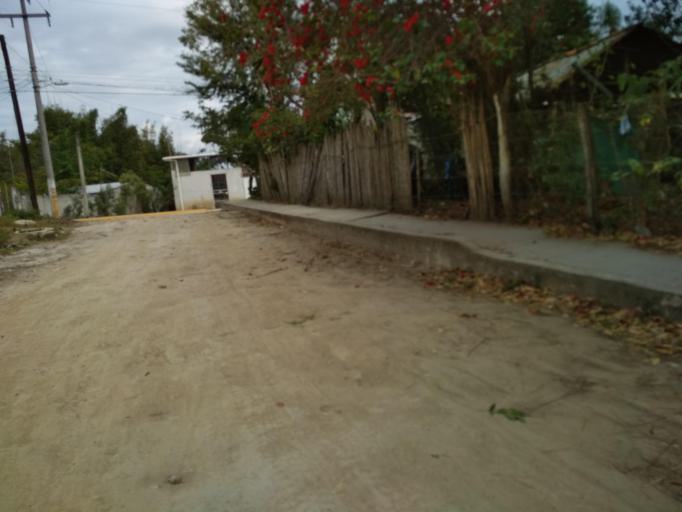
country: MX
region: Veracruz
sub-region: Coatepec
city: Tuzamapan
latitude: 19.3686
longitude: -96.8799
